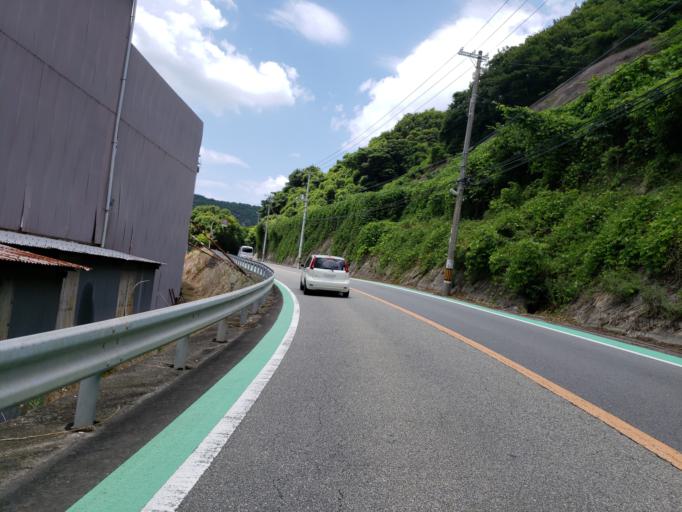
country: JP
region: Hyogo
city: Aioi
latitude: 34.7908
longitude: 134.4704
